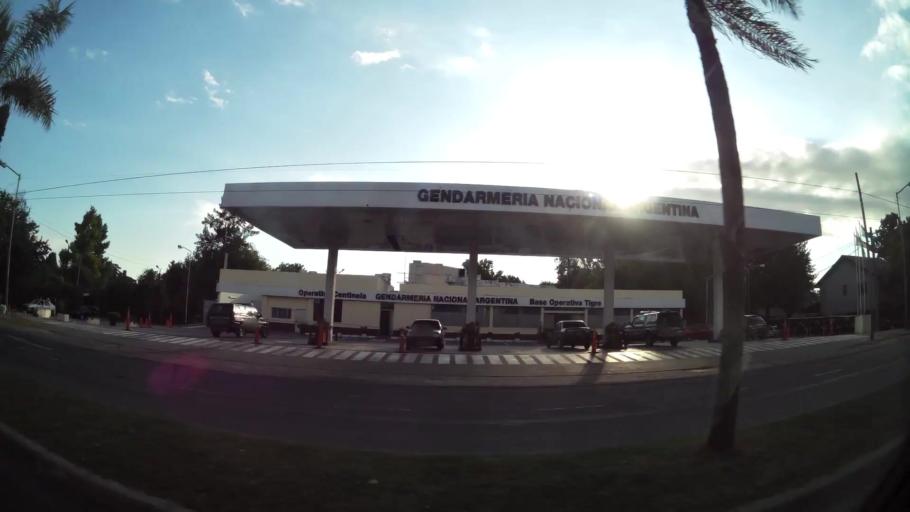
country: AR
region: Buenos Aires
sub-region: Partido de Tigre
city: Tigre
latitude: -34.4653
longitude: -58.6261
